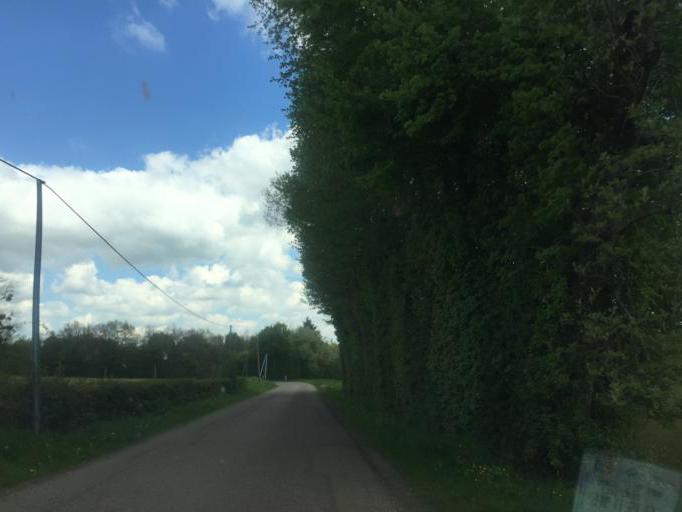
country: FR
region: Bourgogne
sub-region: Departement de l'Yonne
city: Fontenailles
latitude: 47.5494
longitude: 3.3407
